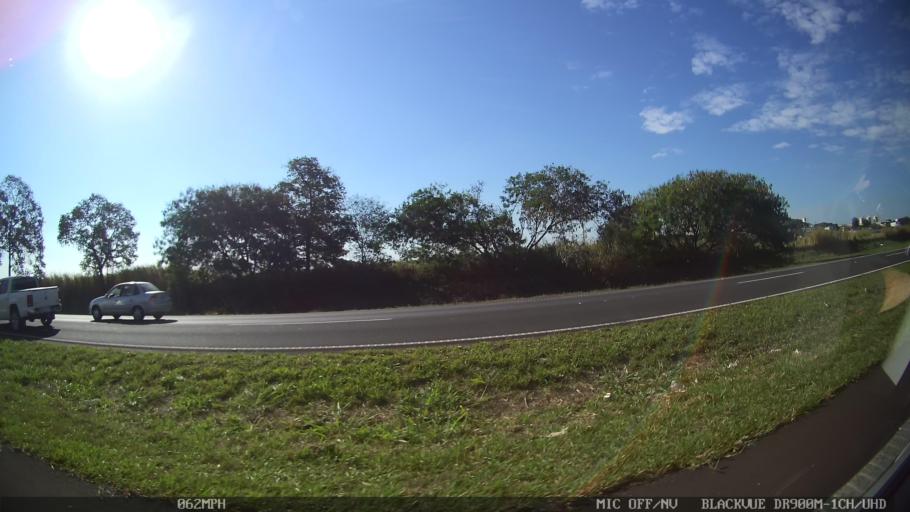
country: BR
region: Sao Paulo
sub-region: Nova Odessa
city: Nova Odessa
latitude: -22.7547
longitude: -47.2653
